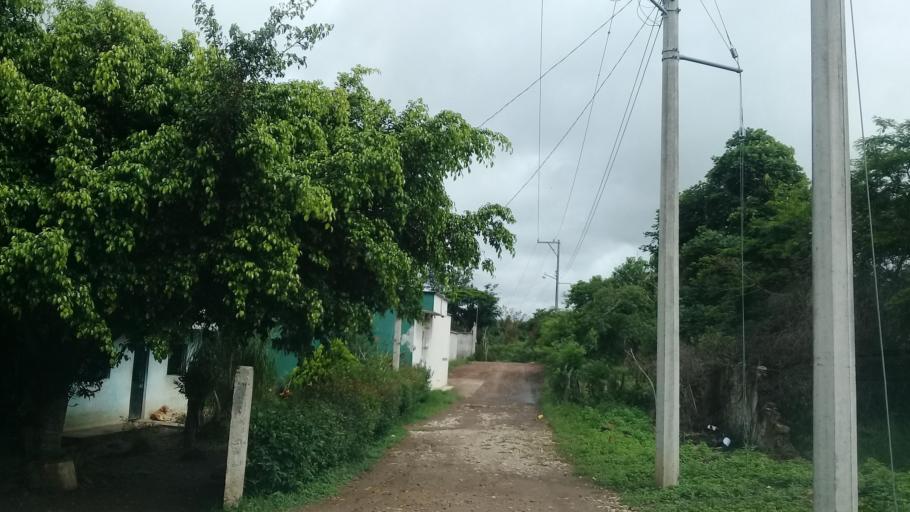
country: MX
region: Veracruz
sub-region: Emiliano Zapata
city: Jacarandas
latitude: 19.4776
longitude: -96.8498
